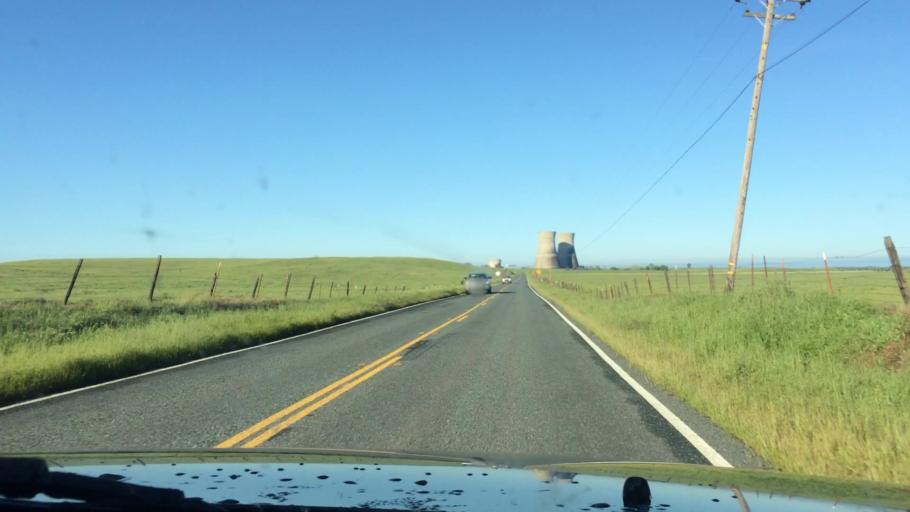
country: US
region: California
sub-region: Sacramento County
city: Clay
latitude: 38.3570
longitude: -121.0929
